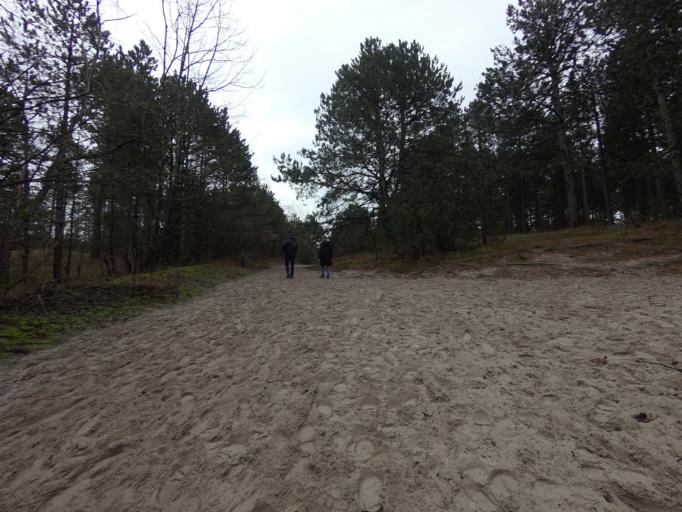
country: NL
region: Zeeland
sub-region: Schouwen-Duiveland
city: Burgh
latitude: 51.6840
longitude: 3.6959
